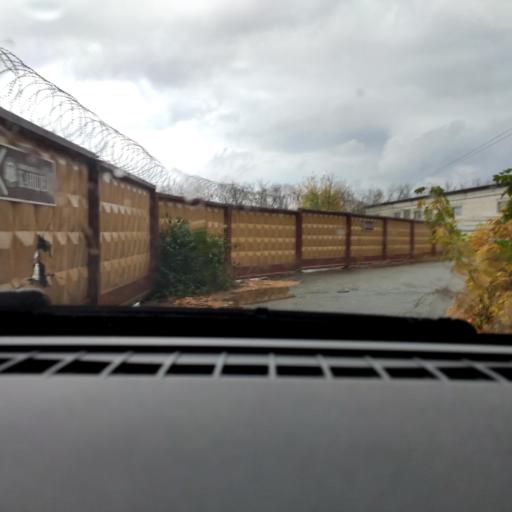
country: RU
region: Voronezj
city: Somovo
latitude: 51.6721
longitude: 39.2968
